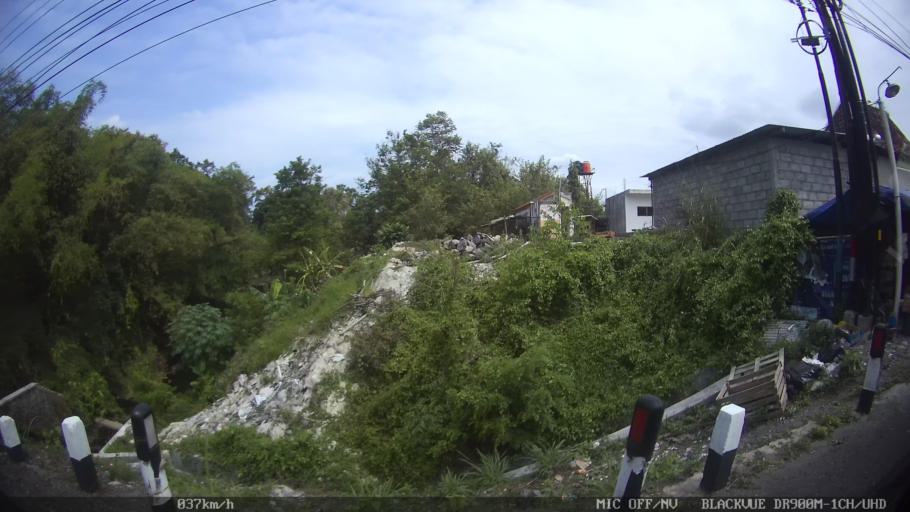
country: ID
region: Daerah Istimewa Yogyakarta
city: Depok
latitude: -7.7316
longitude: 110.4572
